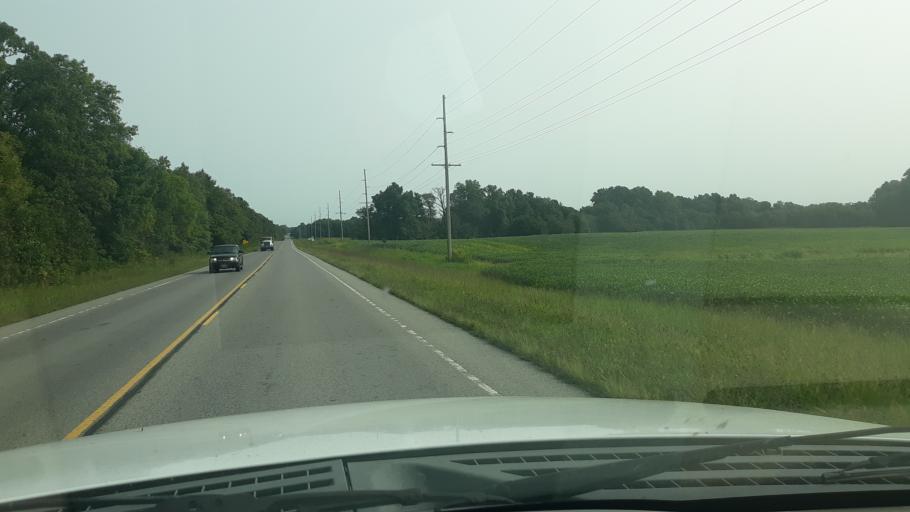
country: US
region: Illinois
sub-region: White County
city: Norris City
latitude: 38.0300
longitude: -88.2560
